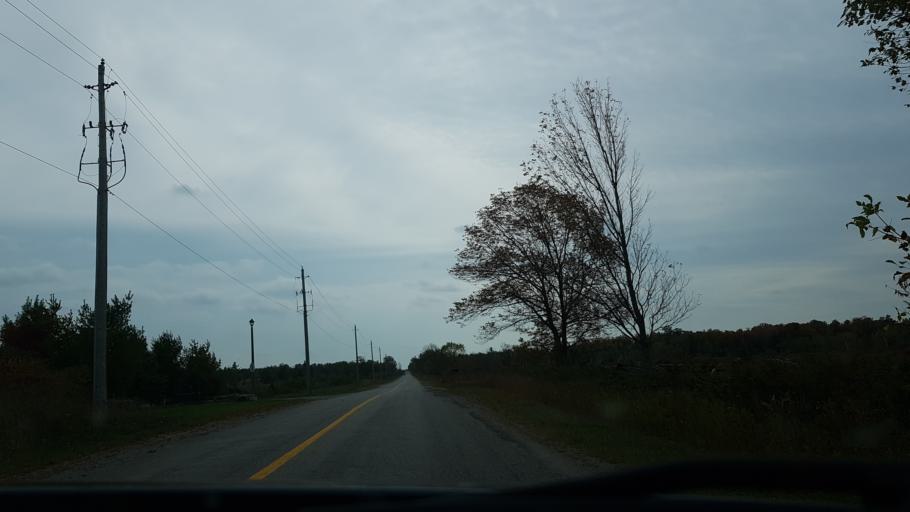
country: CA
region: Ontario
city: Gravenhurst
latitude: 44.6961
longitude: -78.9867
